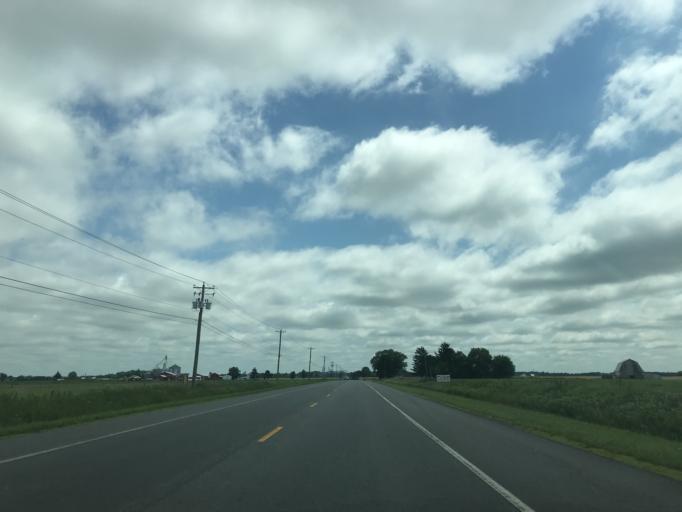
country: US
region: Maryland
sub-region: Caroline County
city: Ridgely
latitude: 38.9303
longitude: -75.9094
